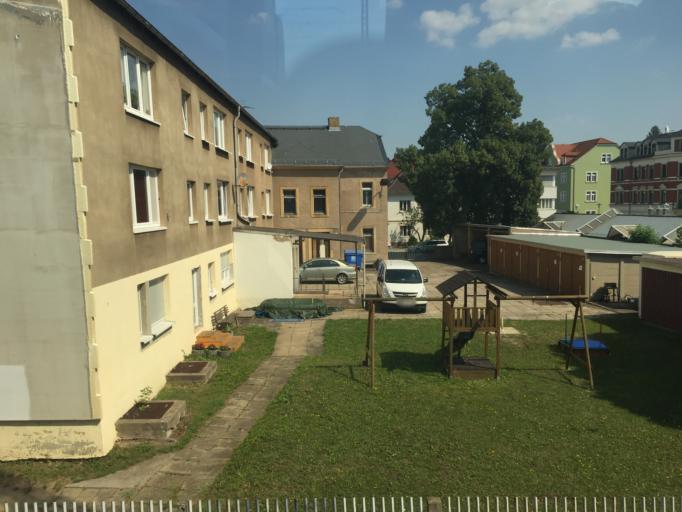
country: DE
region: Saxony
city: Coswig
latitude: 51.1233
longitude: 13.5789
